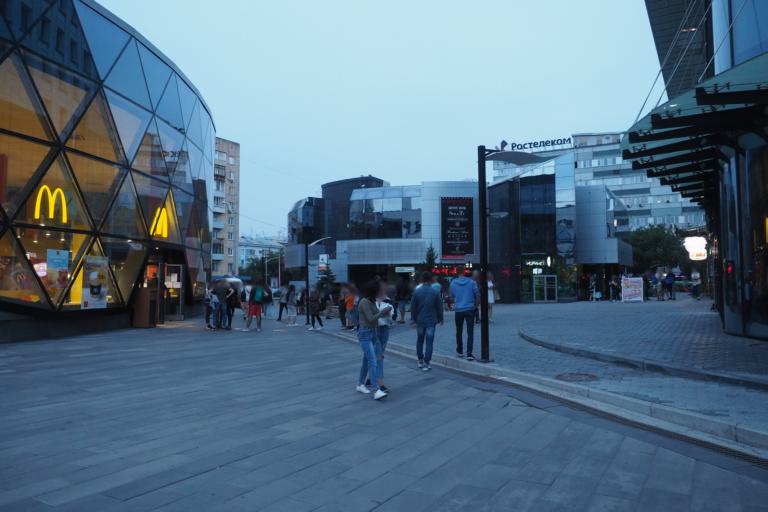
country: RU
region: Krasnoyarskiy
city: Krasnoyarsk
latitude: 56.0093
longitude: 92.8685
